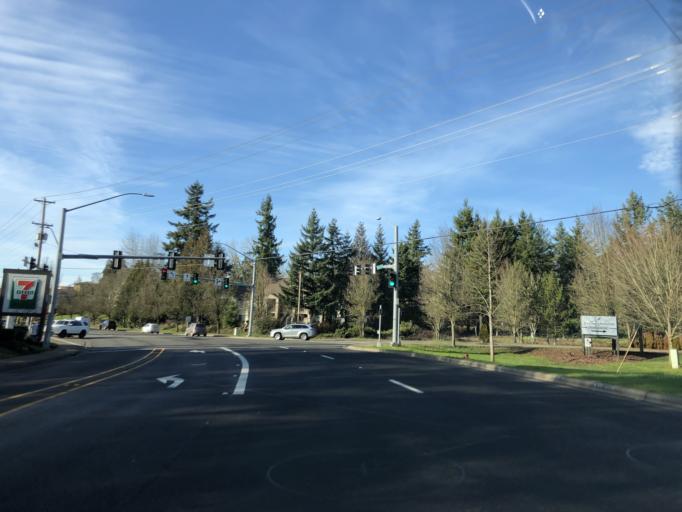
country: US
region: Oregon
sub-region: Washington County
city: Tualatin
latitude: 45.3824
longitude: -122.7444
